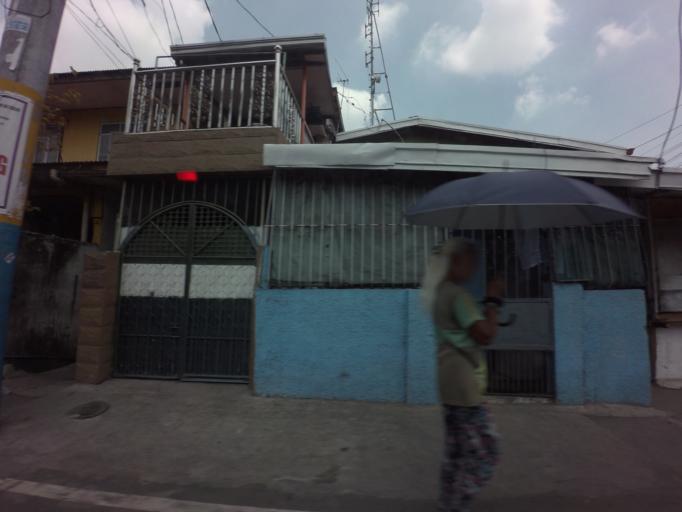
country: PH
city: Sambayanihan People's Village
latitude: 14.4521
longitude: 121.0518
